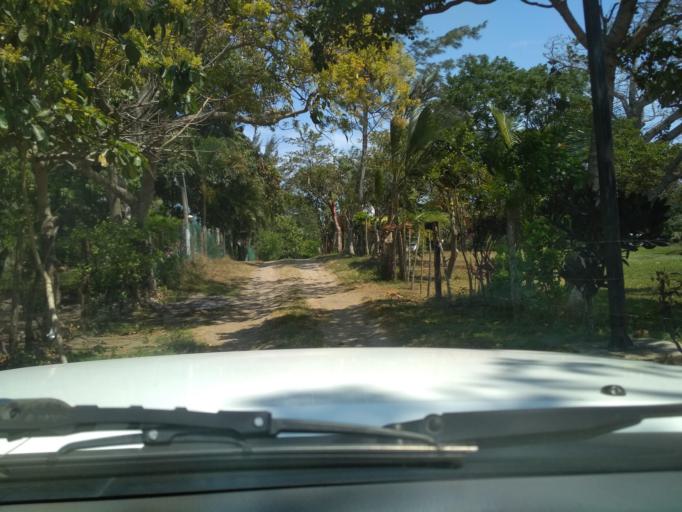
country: MX
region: Veracruz
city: Anton Lizardo
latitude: 19.0018
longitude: -95.9888
